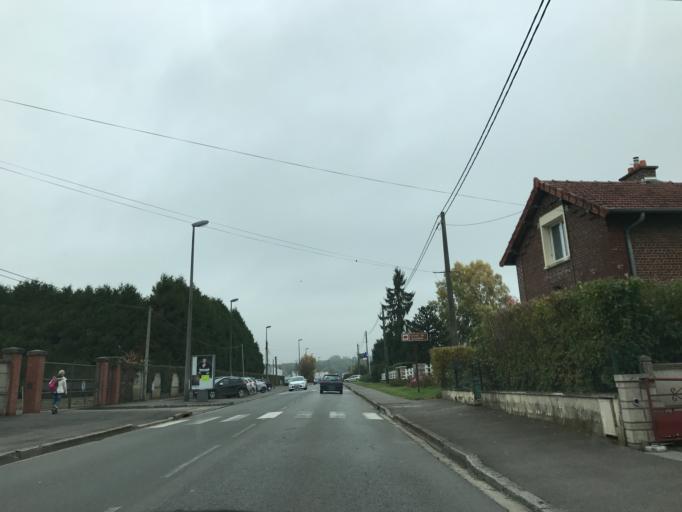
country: FR
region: Picardie
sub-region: Departement de la Somme
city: Peronne
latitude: 49.9368
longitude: 2.9310
